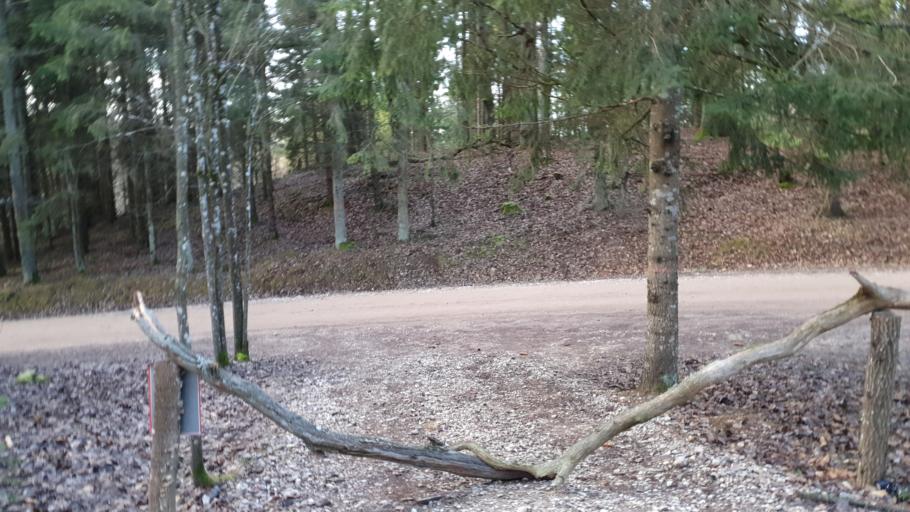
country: LT
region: Vilnius County
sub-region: Vilniaus Rajonas
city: Vievis
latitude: 54.8280
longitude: 24.9471
